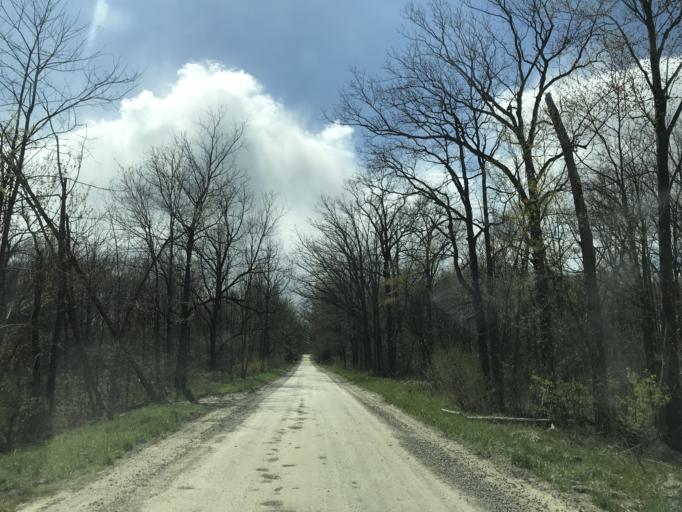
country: US
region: Michigan
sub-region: Livingston County
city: Whitmore Lake
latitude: 42.4034
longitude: -83.7059
